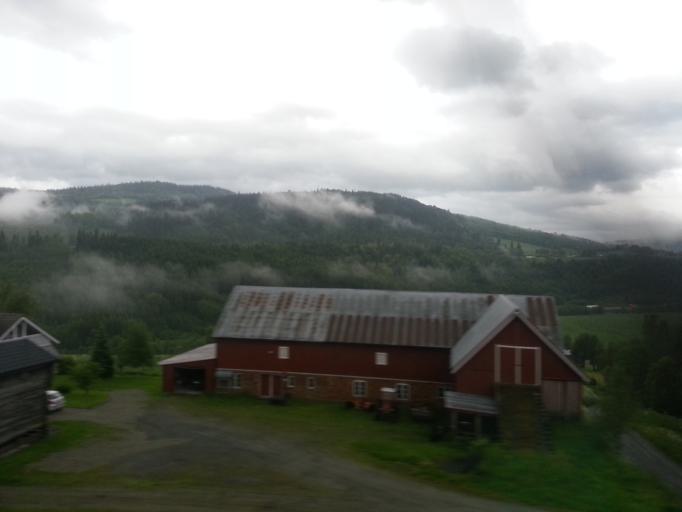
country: NO
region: Sor-Trondelag
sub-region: Midtre Gauldal
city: Storen
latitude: 62.9699
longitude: 10.1863
